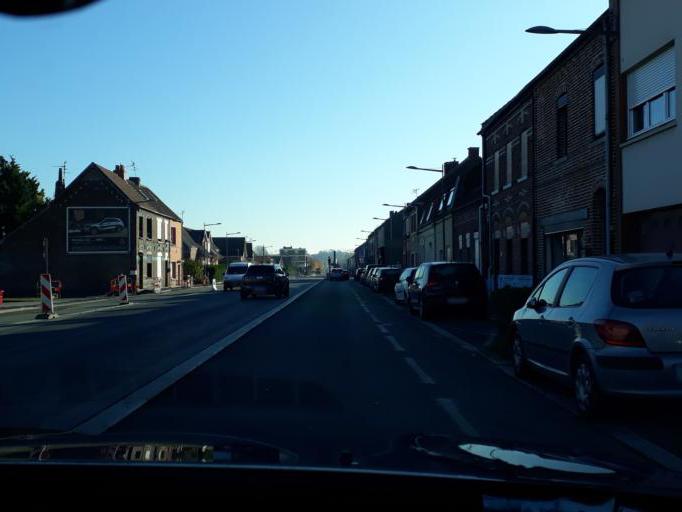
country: FR
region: Nord-Pas-de-Calais
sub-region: Departement du Nord
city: Guesnain
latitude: 50.3463
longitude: 3.1482
